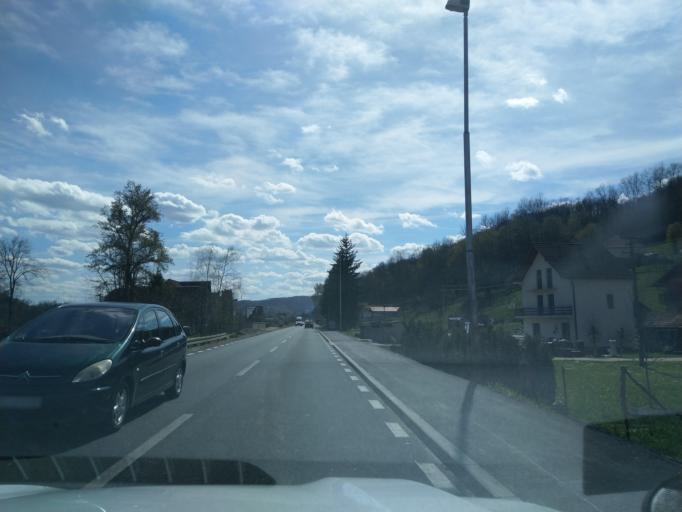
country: RS
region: Central Serbia
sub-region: Zlatiborski Okrug
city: Arilje
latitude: 43.7798
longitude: 20.1032
